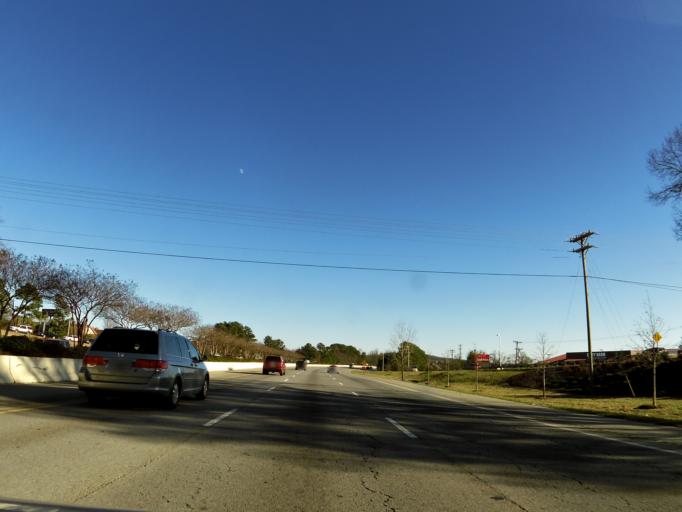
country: US
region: South Carolina
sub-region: Greenville County
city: Wade Hampton
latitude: 34.8542
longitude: -82.3349
